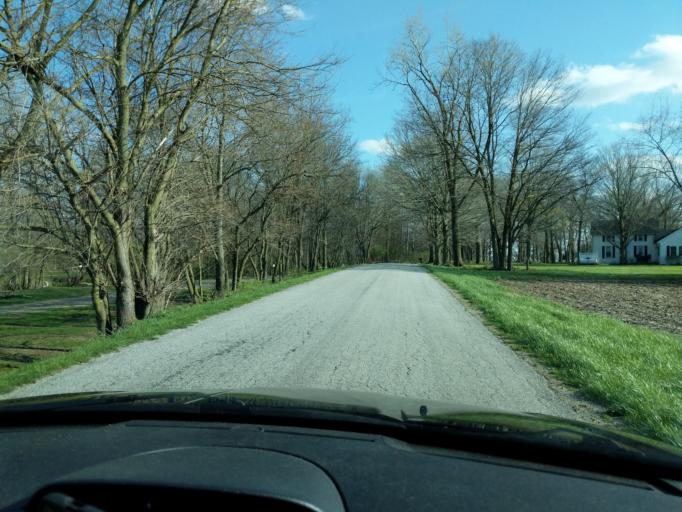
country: US
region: Ohio
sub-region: Champaign County
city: Urbana
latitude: 40.1332
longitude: -83.8106
